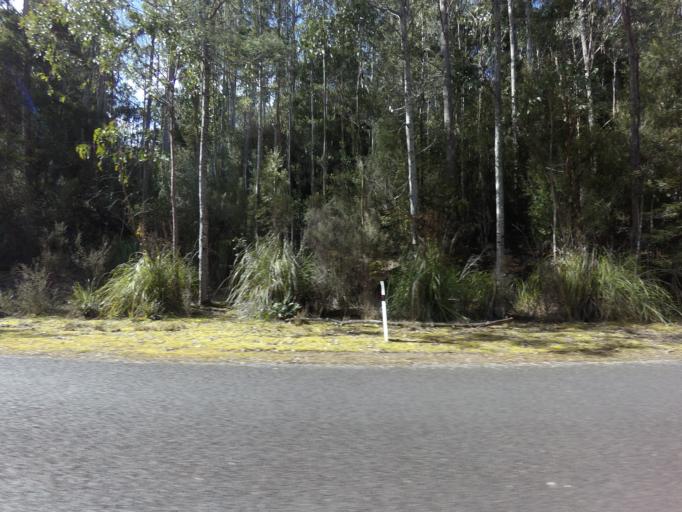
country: AU
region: Tasmania
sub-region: Huon Valley
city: Geeveston
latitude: -42.8256
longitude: 146.3288
